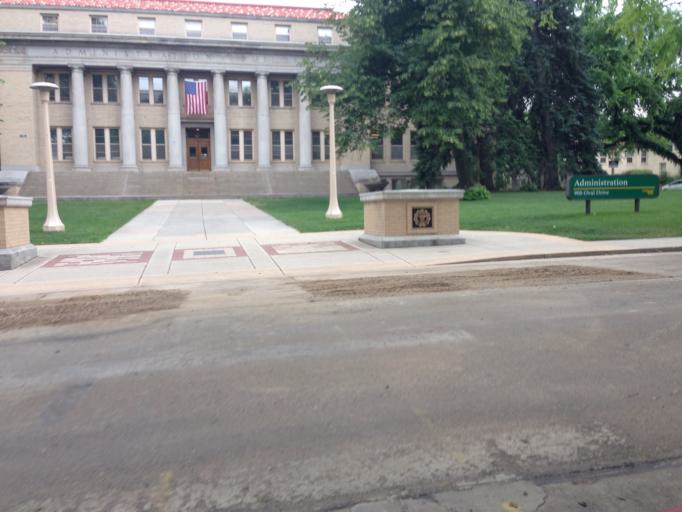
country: US
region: Colorado
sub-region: Larimer County
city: Fort Collins
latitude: 40.5753
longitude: -105.0808
